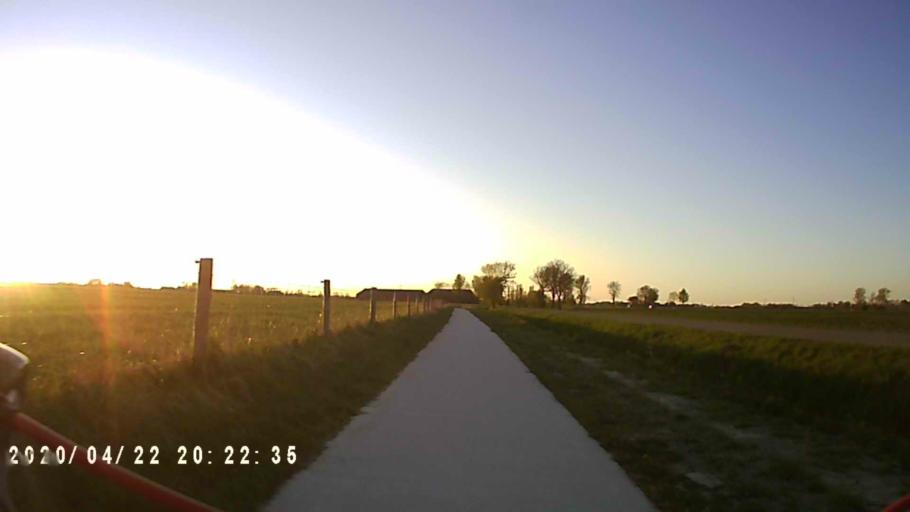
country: NL
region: Groningen
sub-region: Gemeente Winsum
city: Winsum
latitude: 53.3165
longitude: 6.5014
